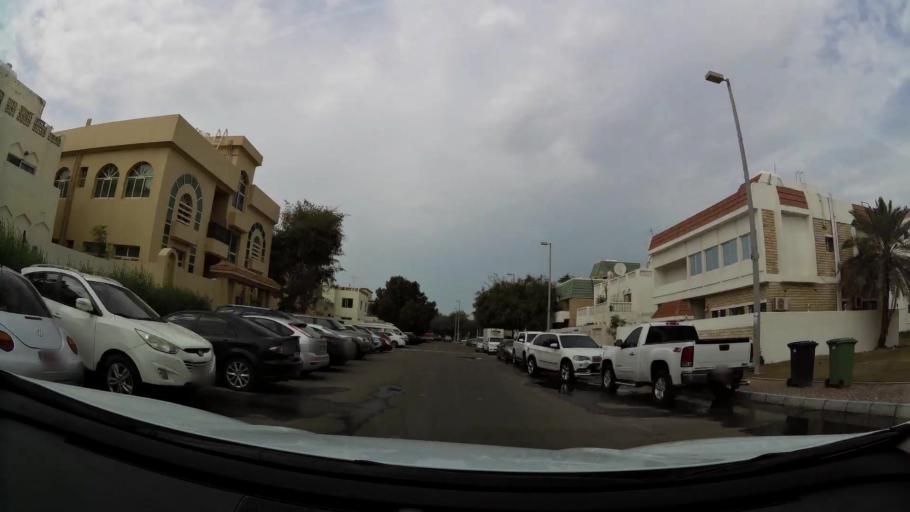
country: AE
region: Abu Dhabi
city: Abu Dhabi
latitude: 24.4359
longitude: 54.4345
